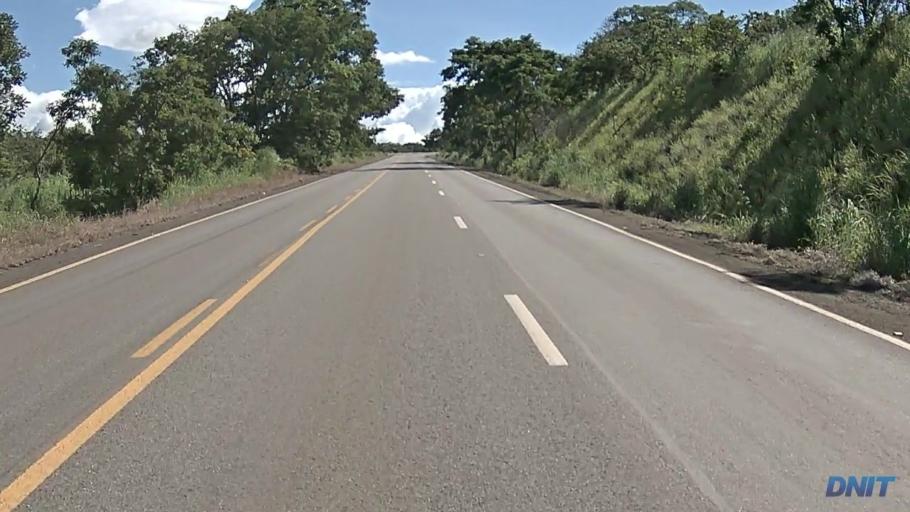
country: BR
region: Goias
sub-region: Padre Bernardo
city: Padre Bernardo
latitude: -15.1902
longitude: -48.4359
